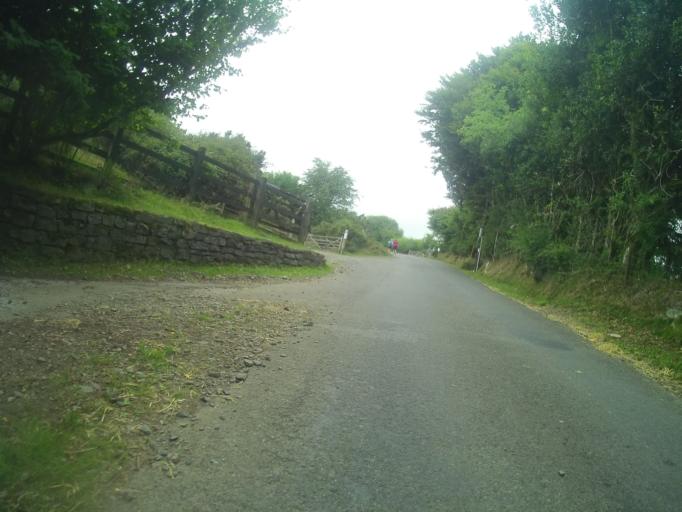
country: GB
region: England
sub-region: Devon
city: Buckfastleigh
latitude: 50.5149
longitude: -3.8379
